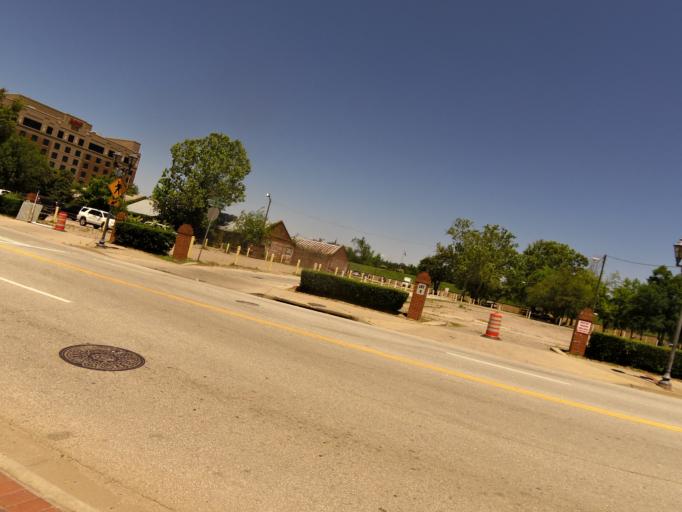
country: US
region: Georgia
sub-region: Richmond County
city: Augusta
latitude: 33.4769
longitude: -81.9657
